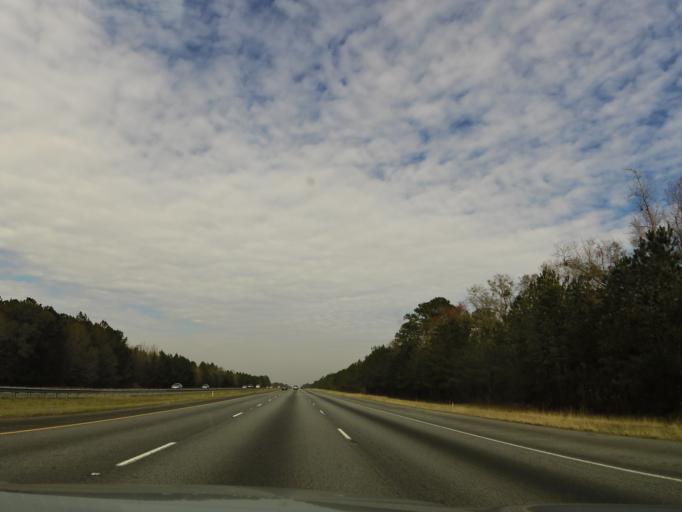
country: US
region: Georgia
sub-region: Liberty County
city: Midway
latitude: 31.6033
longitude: -81.4199
